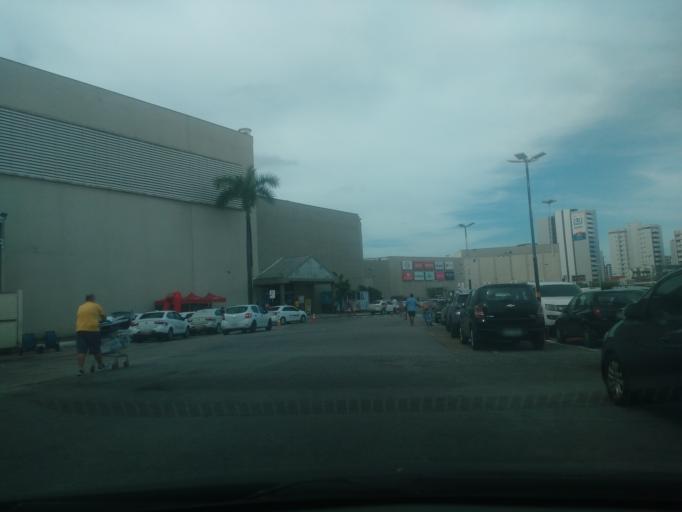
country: BR
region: Alagoas
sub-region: Maceio
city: Maceio
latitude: -9.6492
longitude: -35.7158
